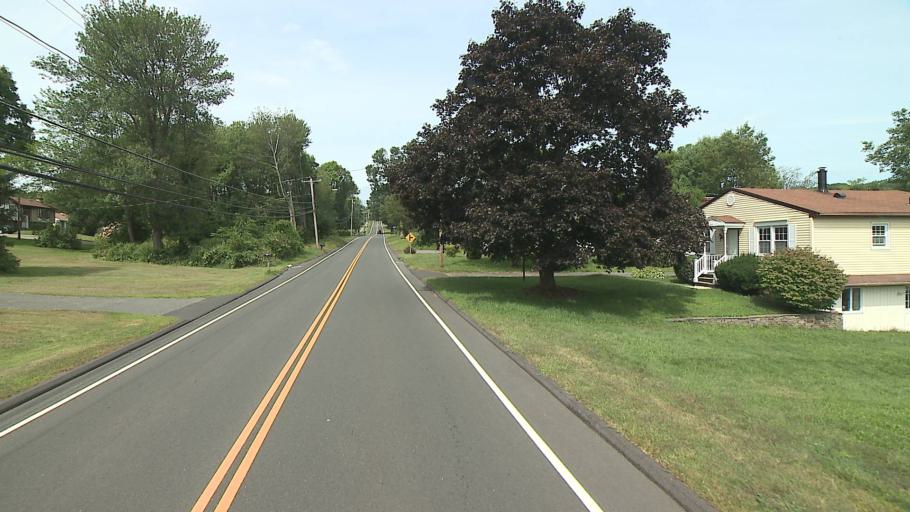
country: US
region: Connecticut
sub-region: Litchfield County
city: Plymouth
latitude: 41.6535
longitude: -73.0520
